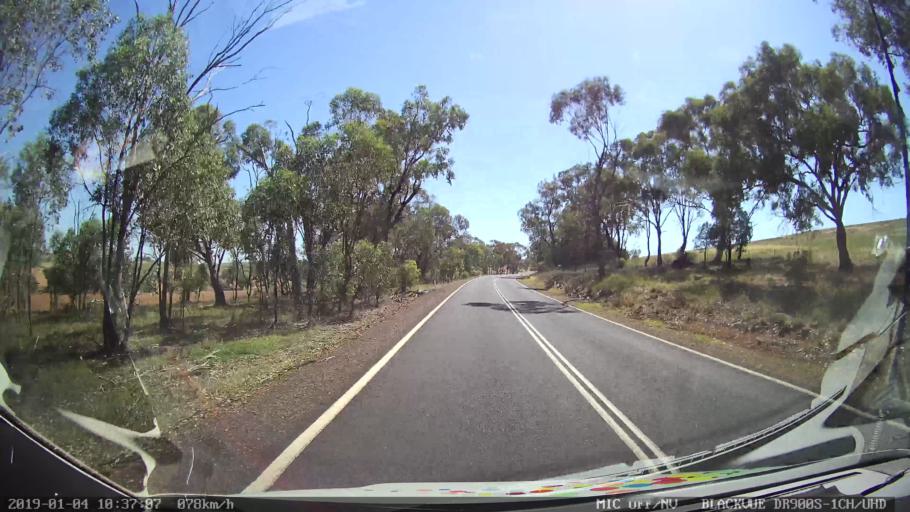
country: AU
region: New South Wales
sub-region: Cabonne
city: Canowindra
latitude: -33.2981
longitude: 148.6910
